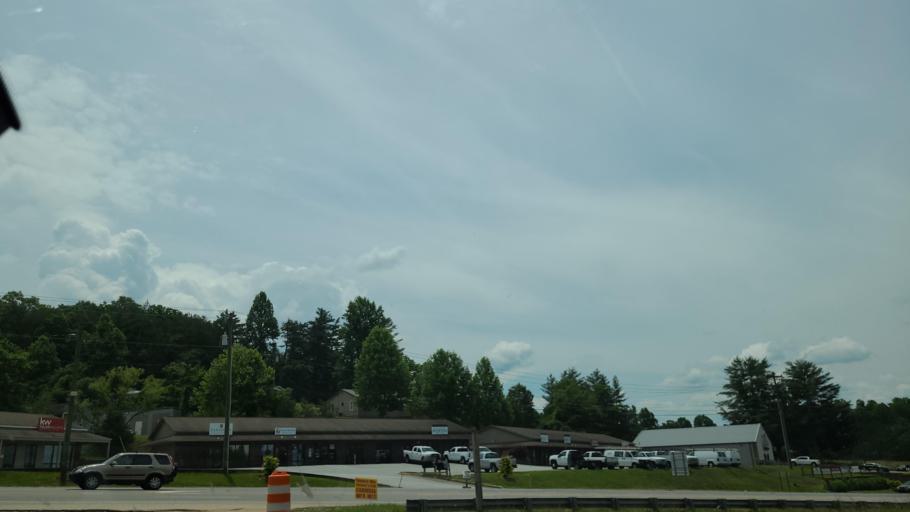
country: US
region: North Carolina
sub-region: Macon County
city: Franklin
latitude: 35.1764
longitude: -83.3546
